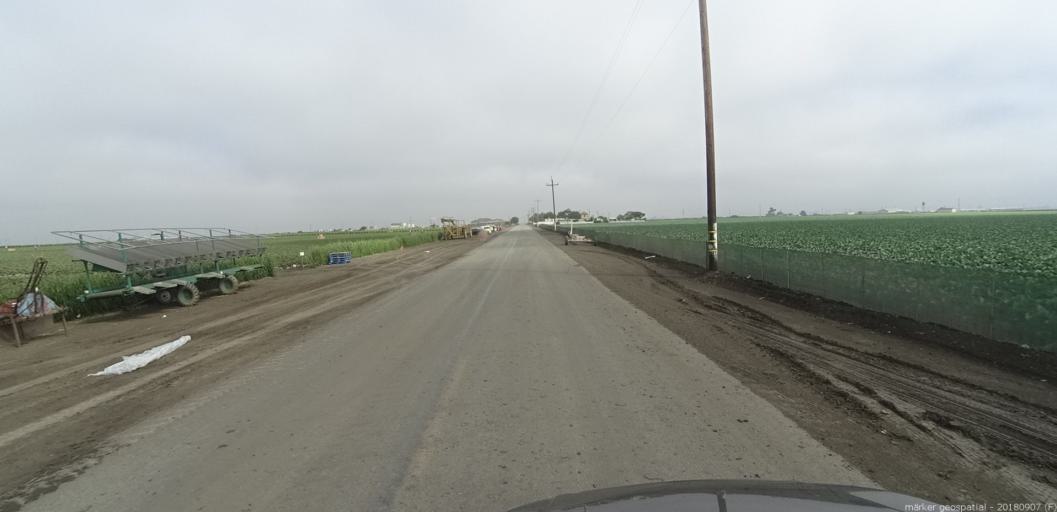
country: US
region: California
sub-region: Monterey County
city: Boronda
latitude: 36.6865
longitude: -121.7078
